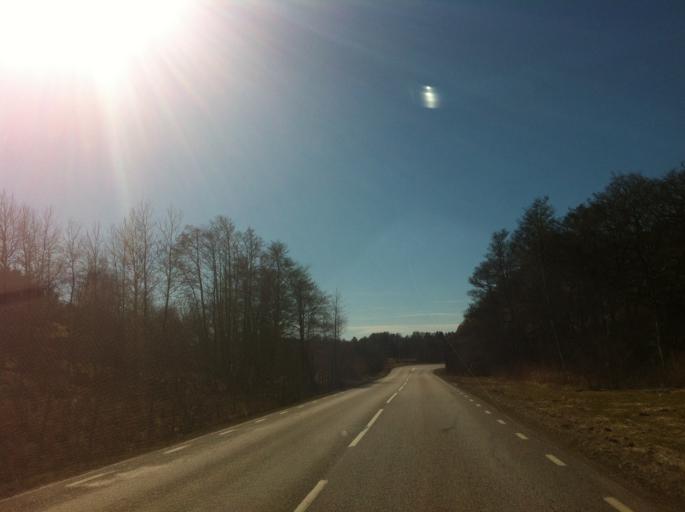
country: SE
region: Vaestra Goetaland
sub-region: Sotenas Kommun
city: Hunnebostrand
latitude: 58.4160
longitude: 11.3762
